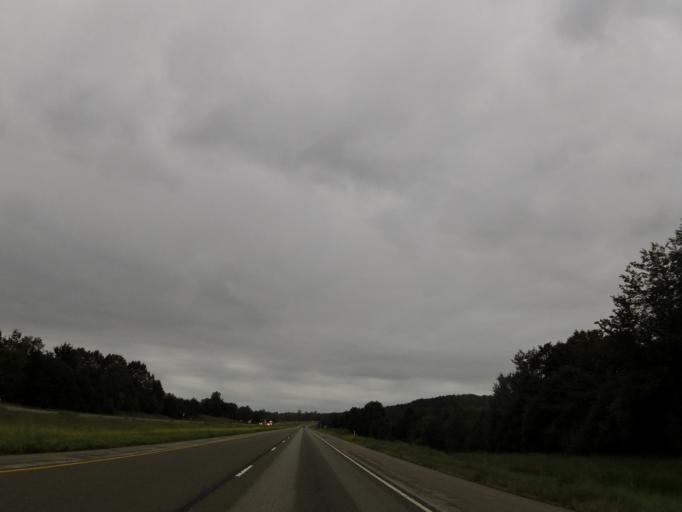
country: US
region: Illinois
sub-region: Johnson County
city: Vienna
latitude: 37.3332
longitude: -88.7774
